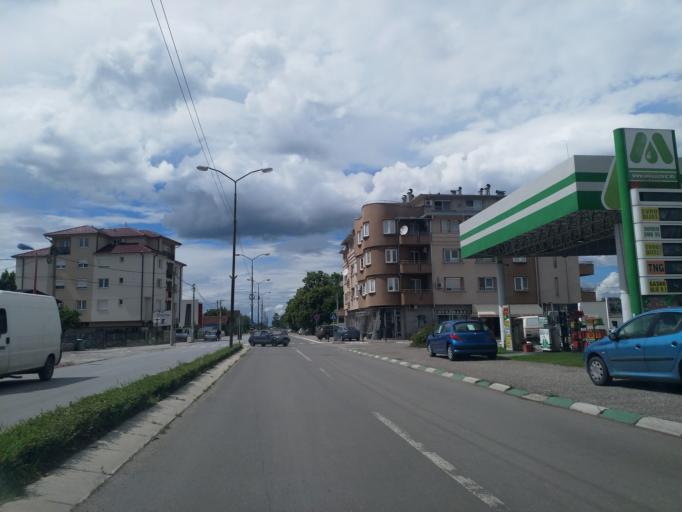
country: RS
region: Central Serbia
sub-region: Pomoravski Okrug
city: Paracin
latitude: 43.8670
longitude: 21.4060
